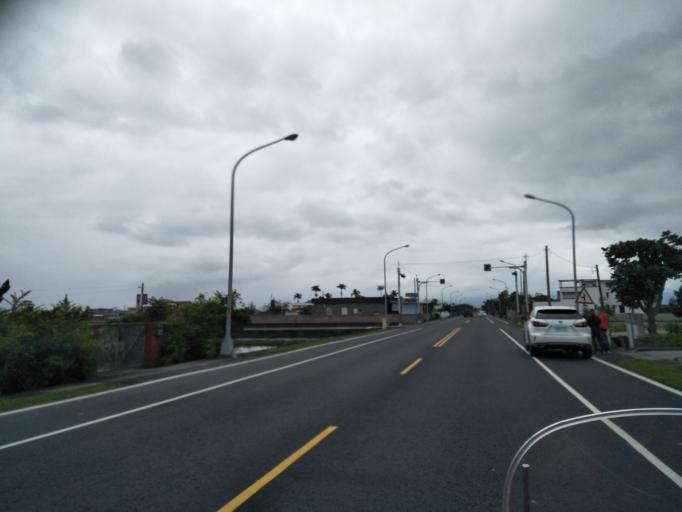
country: TW
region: Taiwan
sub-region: Yilan
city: Yilan
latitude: 24.8036
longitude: 121.7890
